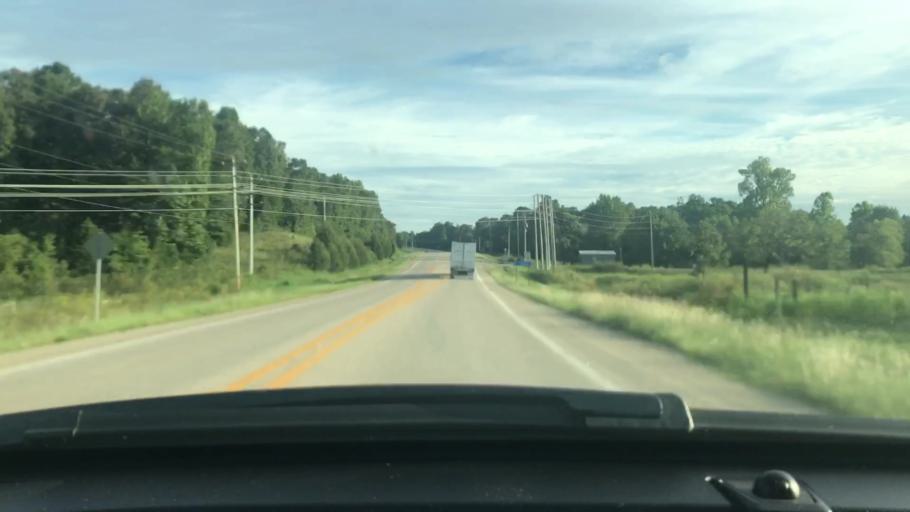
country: US
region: Arkansas
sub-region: Lawrence County
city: Hoxie
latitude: 36.1365
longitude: -91.1582
